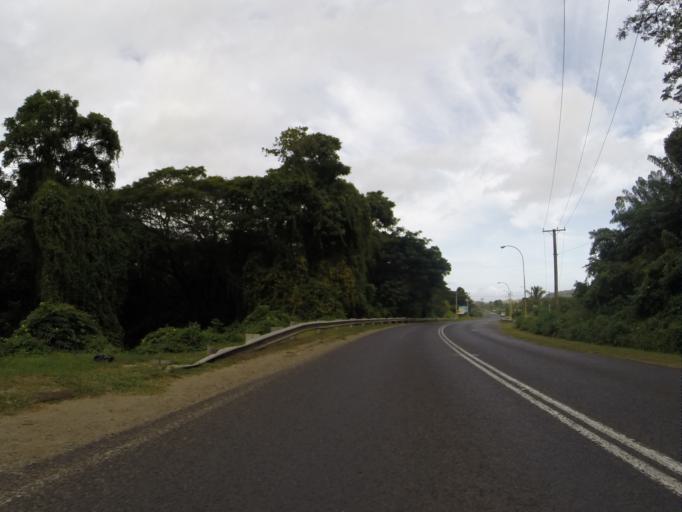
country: FJ
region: Western
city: Nadi
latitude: -18.1503
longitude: 177.5003
